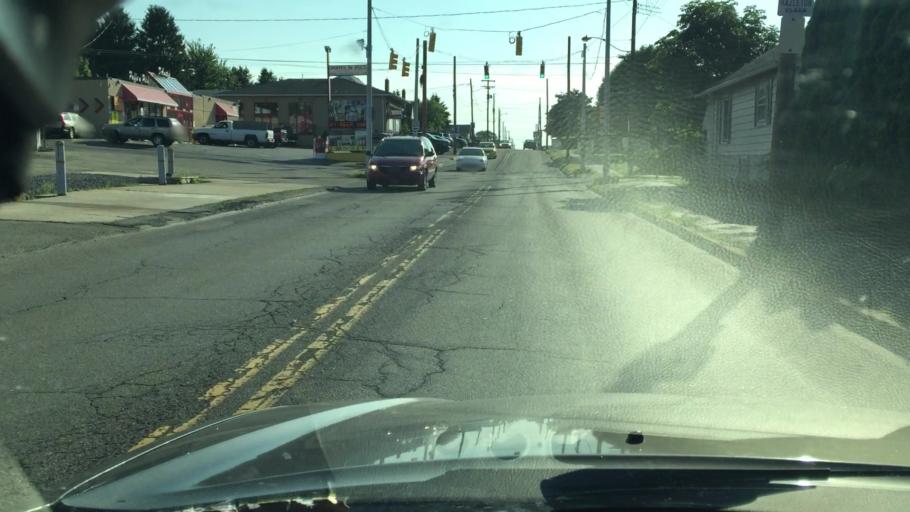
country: US
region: Pennsylvania
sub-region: Luzerne County
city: West Hazleton
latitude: 40.9666
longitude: -75.9861
